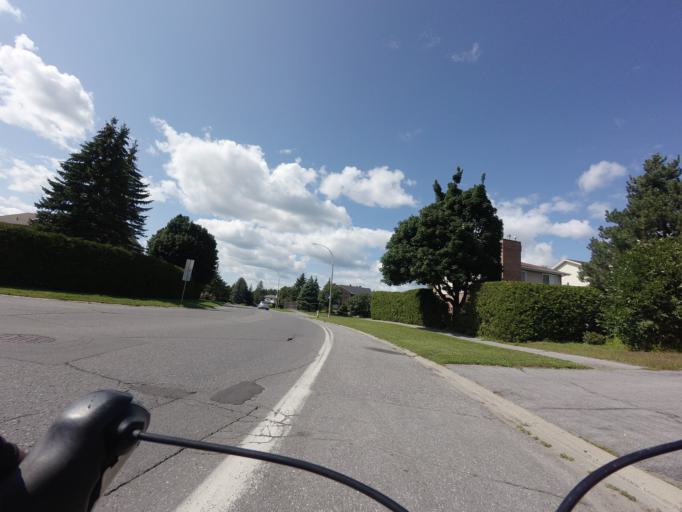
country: CA
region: Ontario
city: Bells Corners
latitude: 45.2915
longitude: -75.8636
